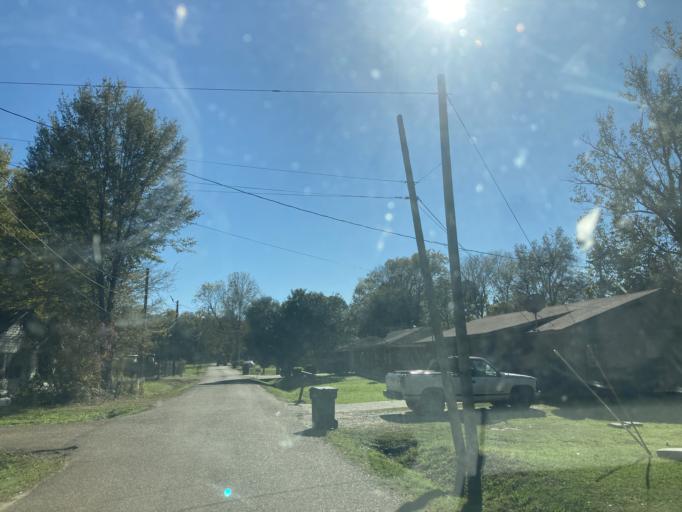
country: US
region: Mississippi
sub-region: Yazoo County
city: Yazoo City
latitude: 32.8436
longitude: -90.4306
